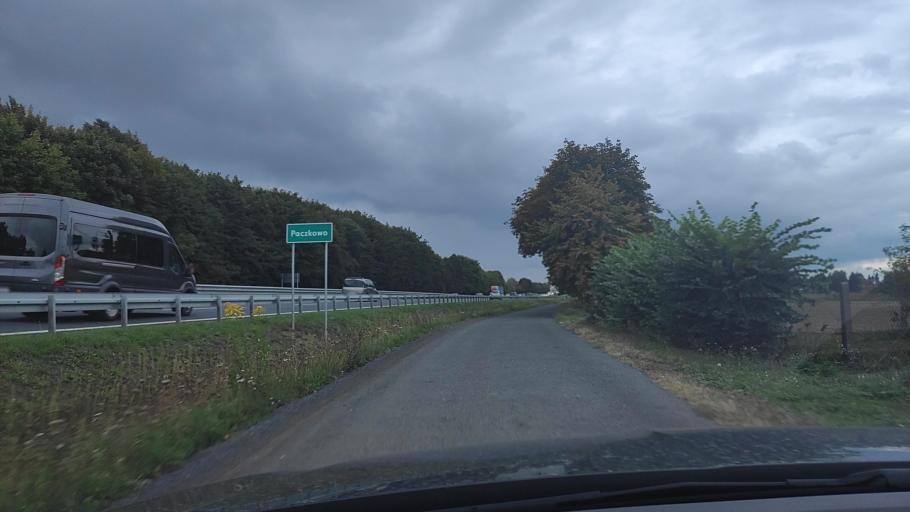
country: PL
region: Greater Poland Voivodeship
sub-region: Powiat poznanski
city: Kostrzyn
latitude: 52.3962
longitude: 17.1720
